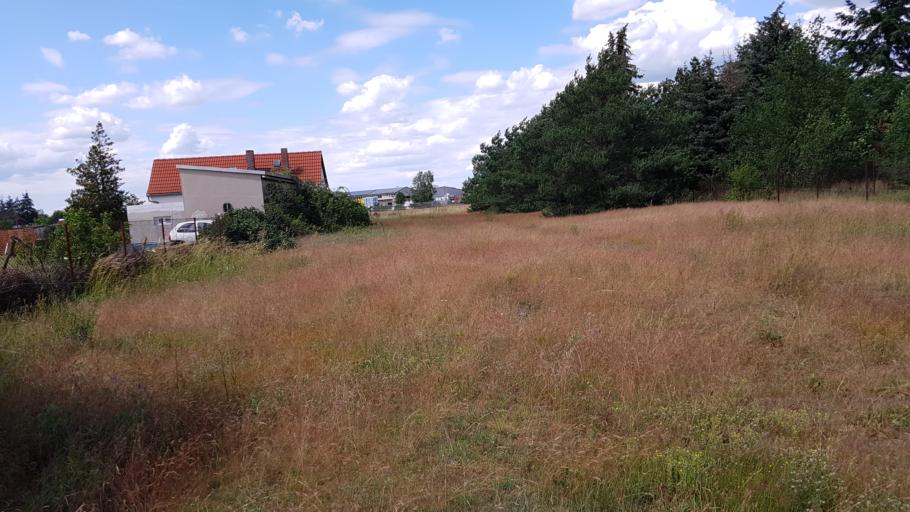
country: DE
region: Brandenburg
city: Finsterwalde
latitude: 51.6171
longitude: 13.7280
